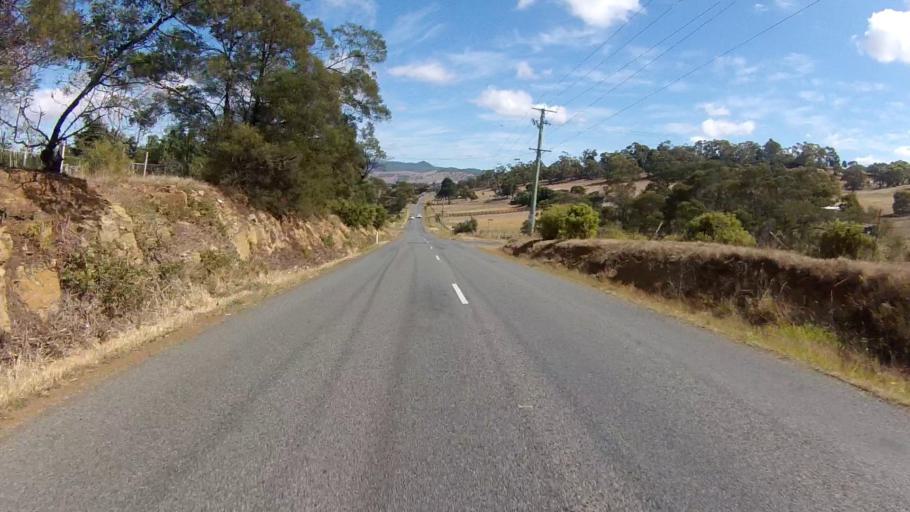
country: AU
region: Tasmania
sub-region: Brighton
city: Bridgewater
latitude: -42.7134
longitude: 147.2728
